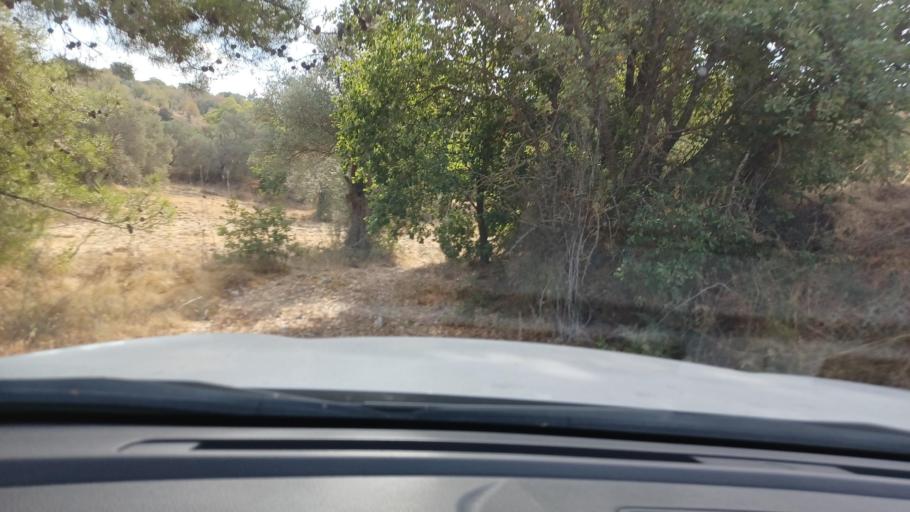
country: CY
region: Pafos
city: Polis
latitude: 35.0071
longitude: 32.5129
